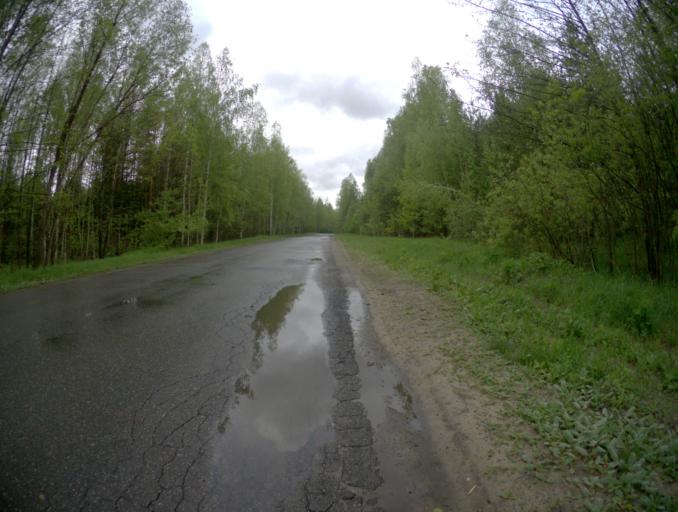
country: RU
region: Vladimir
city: Zolotkovo
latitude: 55.3448
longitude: 40.9888
